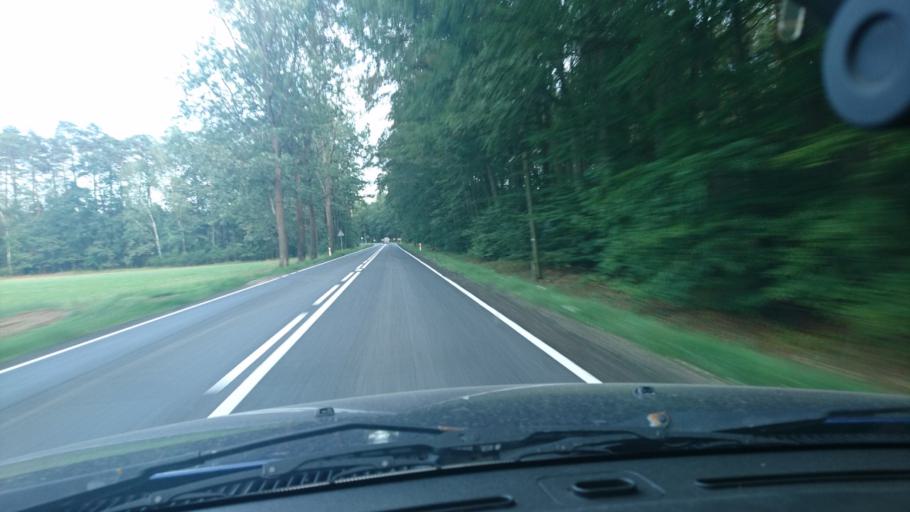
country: PL
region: Opole Voivodeship
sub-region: Powiat oleski
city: Olesno
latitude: 50.8516
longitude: 18.4675
